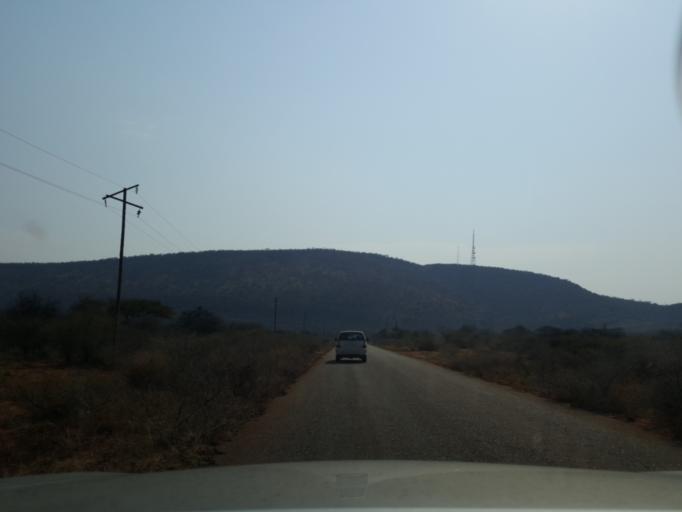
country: BW
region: South East
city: Lobatse
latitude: -25.2877
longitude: 25.8574
